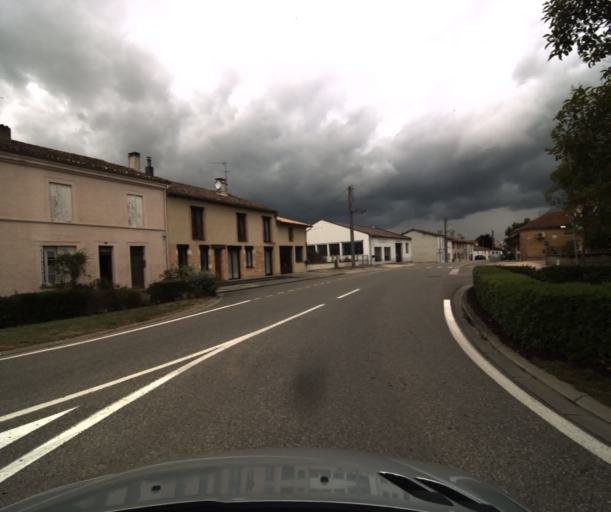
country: FR
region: Midi-Pyrenees
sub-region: Departement du Tarn-et-Garonne
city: Lavit
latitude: 43.9563
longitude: 0.9178
